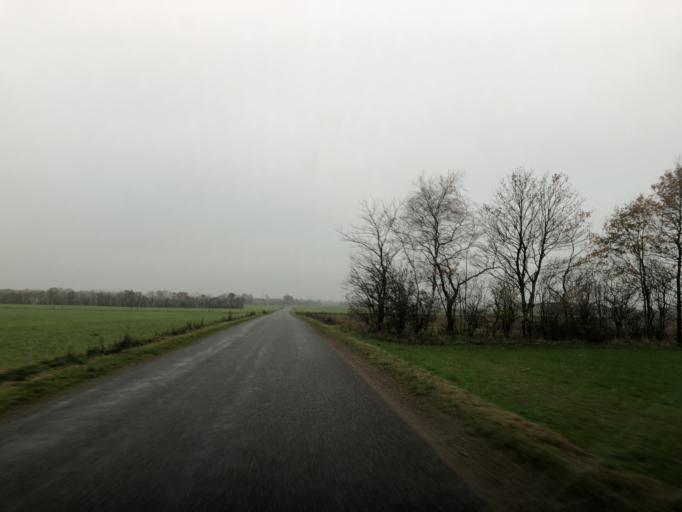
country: DK
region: Central Jutland
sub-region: Herning Kommune
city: Avlum
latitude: 56.2484
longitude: 8.8270
